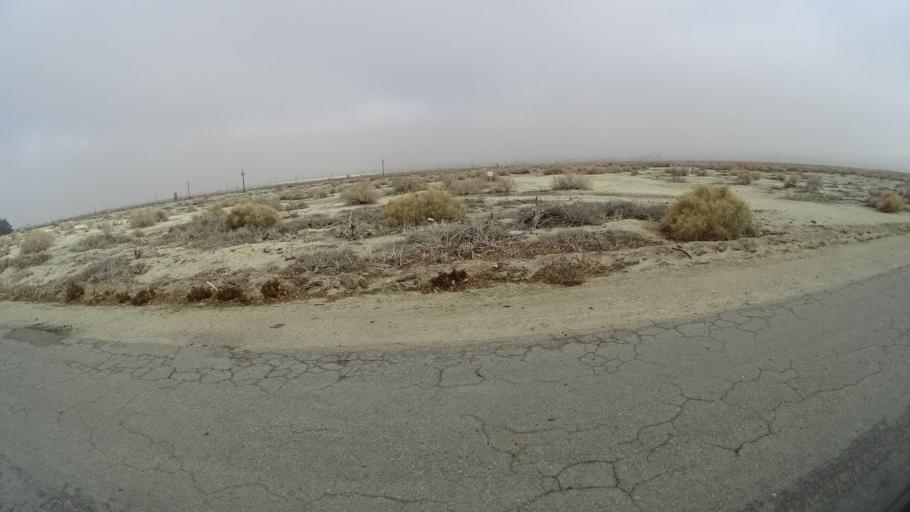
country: US
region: California
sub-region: Kern County
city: Maricopa
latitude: 35.0550
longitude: -119.3952
